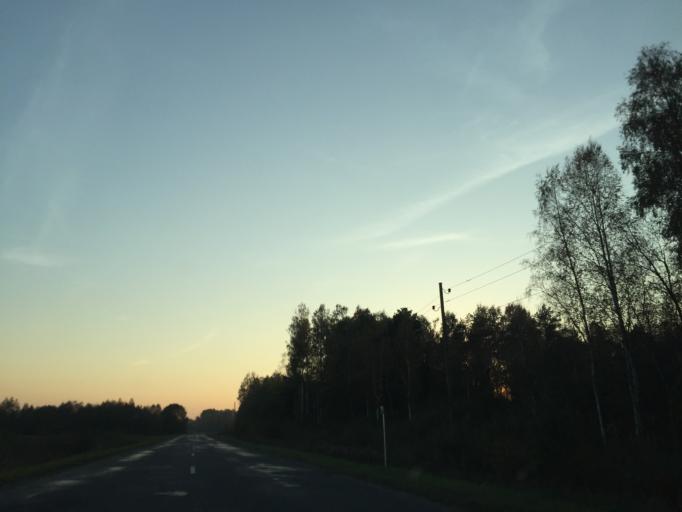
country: LT
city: Skuodas
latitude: 56.3433
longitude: 21.5788
